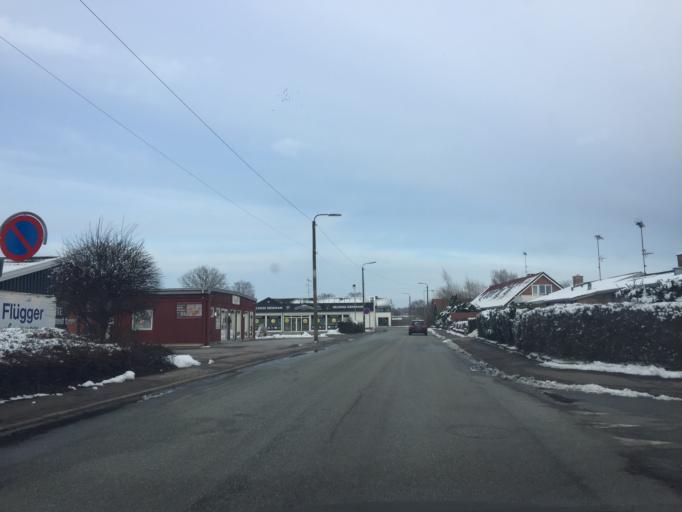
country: DK
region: Capital Region
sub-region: Gribskov Kommune
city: Helsinge
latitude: 56.0185
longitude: 12.1987
